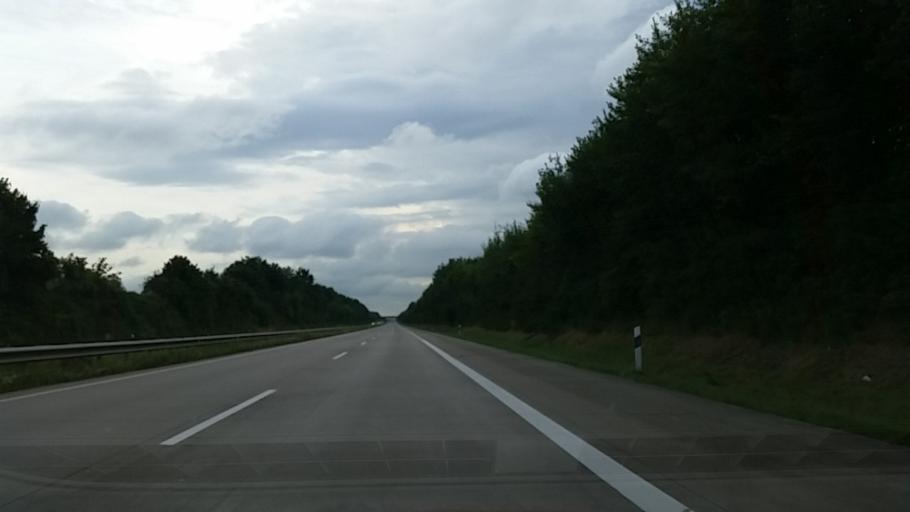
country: DE
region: Schleswig-Holstein
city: Mohnsen
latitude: 53.5608
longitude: 10.4429
